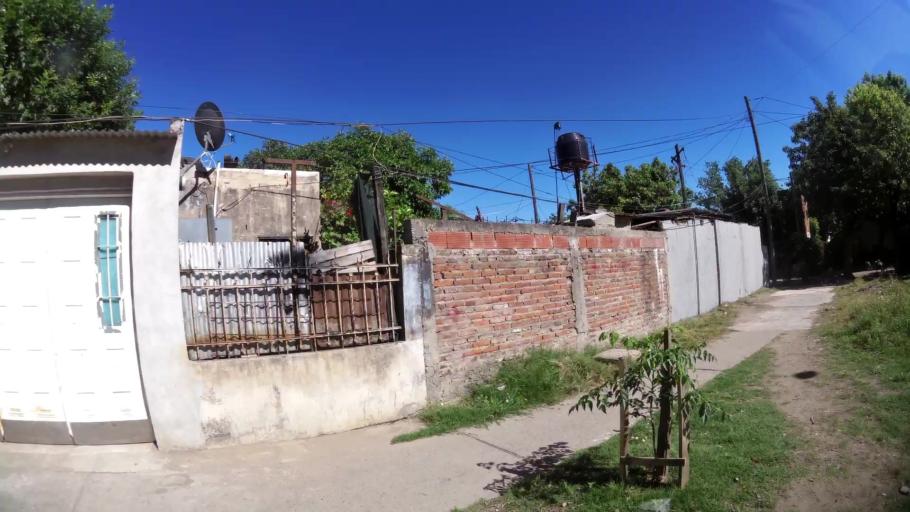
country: AR
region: Santa Fe
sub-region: Departamento de Rosario
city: Rosario
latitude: -32.9541
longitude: -60.6892
